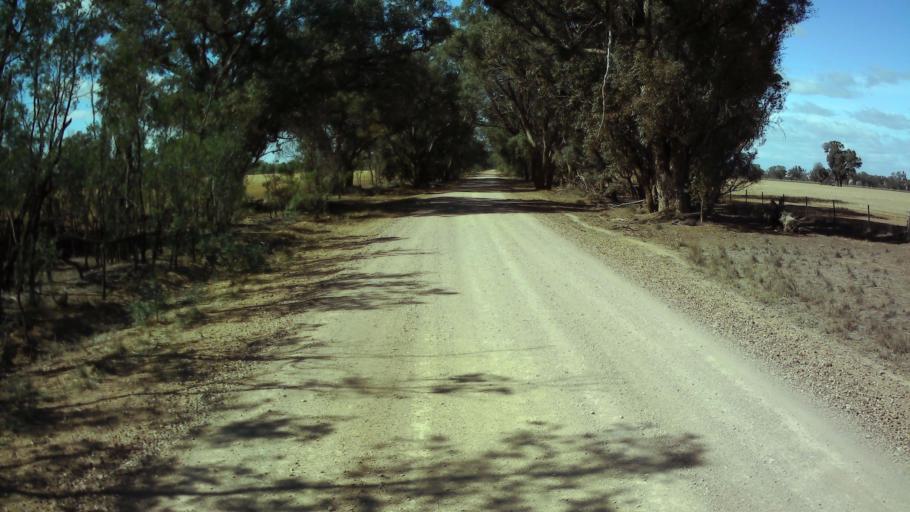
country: AU
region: New South Wales
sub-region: Weddin
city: Grenfell
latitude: -34.0361
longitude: 148.3166
